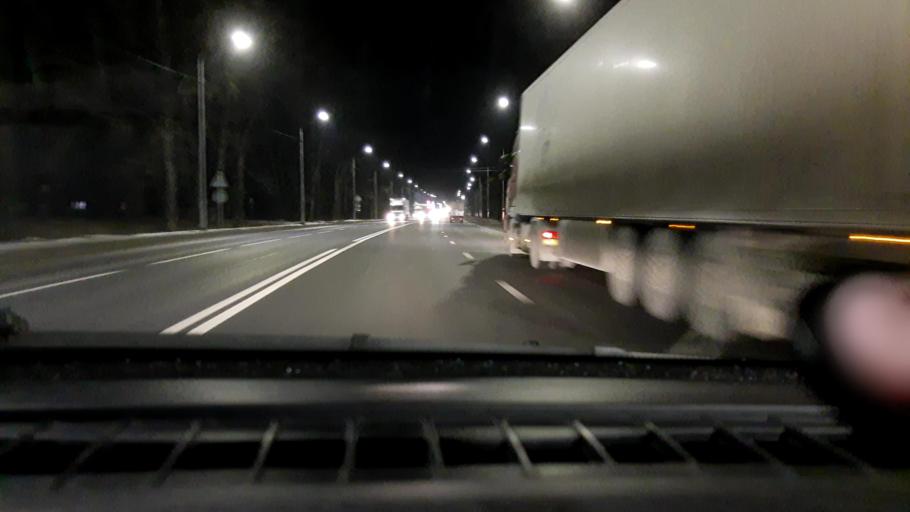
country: RU
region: Nizjnij Novgorod
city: Lyskovo
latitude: 56.0137
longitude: 45.0268
